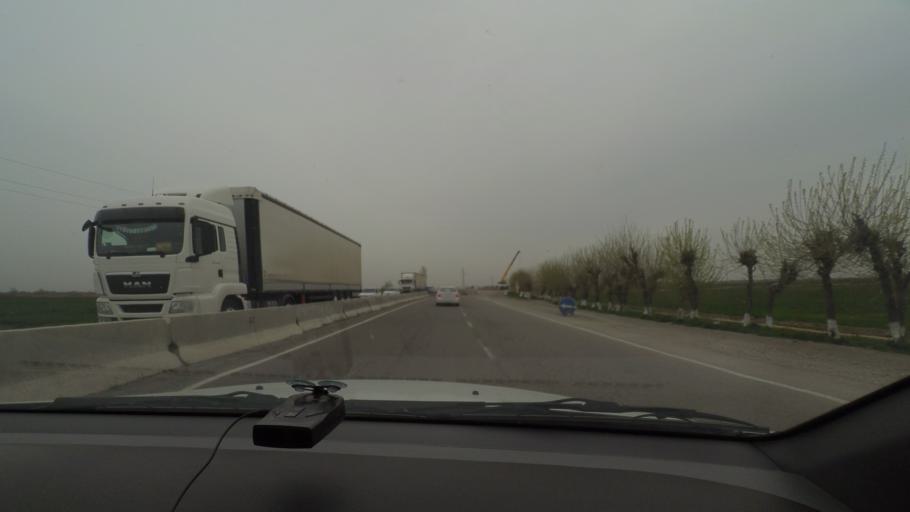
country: KZ
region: Ongtustik Qazaqstan
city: Myrzakent
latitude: 40.5607
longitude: 68.3826
